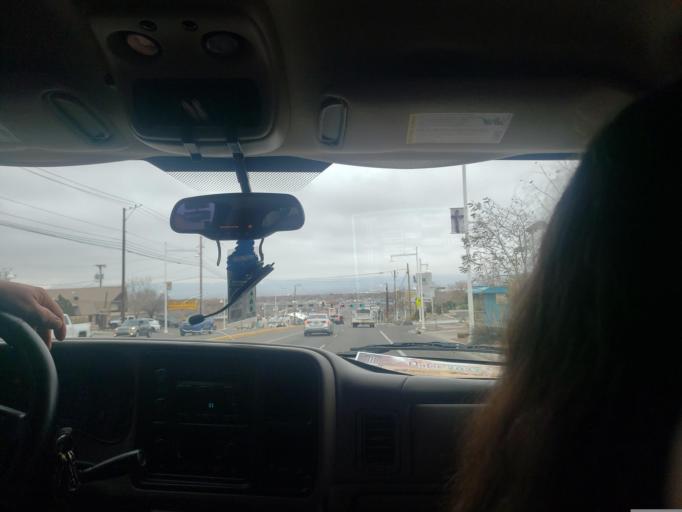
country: US
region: New Mexico
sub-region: Bernalillo County
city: Albuquerque
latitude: 35.0826
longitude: -106.6978
